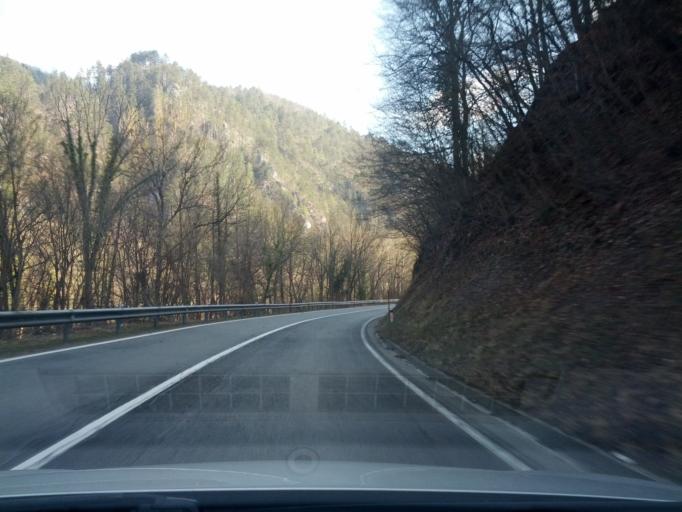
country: SI
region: Zagorje ob Savi
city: Izlake
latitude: 46.0923
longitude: 14.9075
